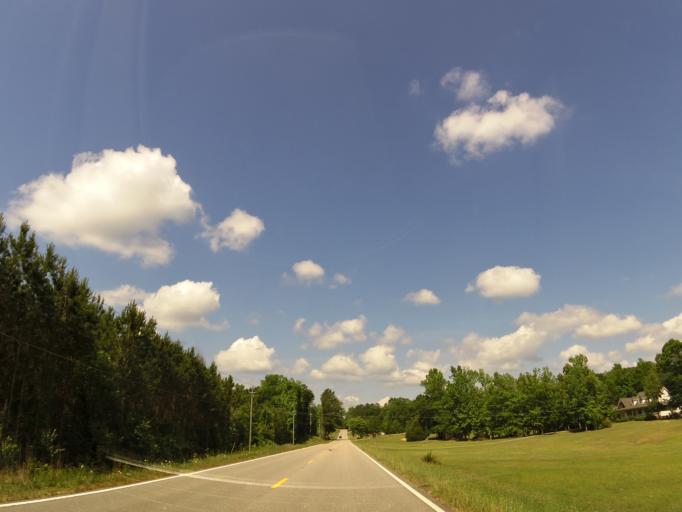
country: US
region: Alabama
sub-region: Marion County
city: Guin
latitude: 34.0102
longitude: -87.8450
